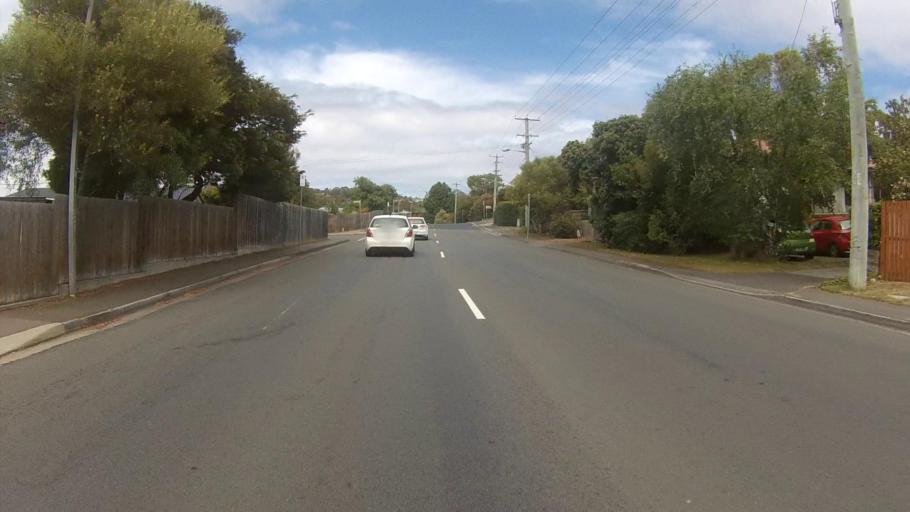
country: AU
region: Tasmania
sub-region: Kingborough
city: Blackmans Bay
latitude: -43.0016
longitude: 147.3197
